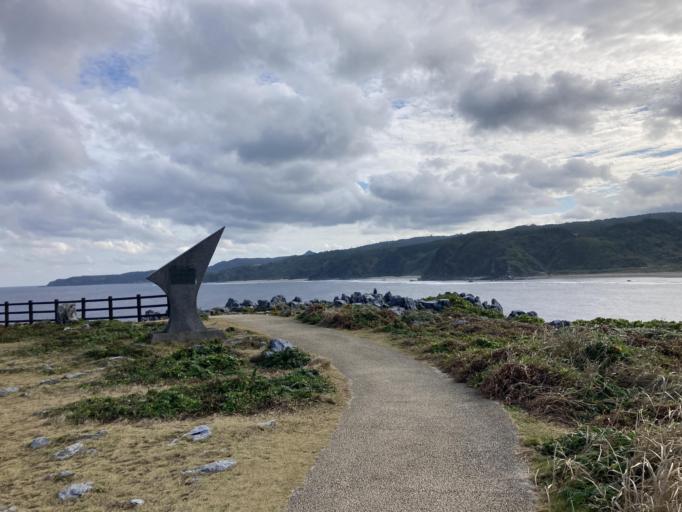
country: JP
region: Okinawa
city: Nago
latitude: 26.8722
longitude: 128.2644
